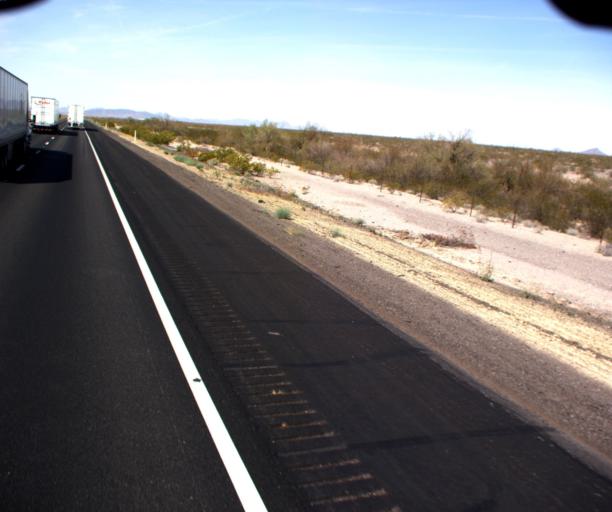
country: US
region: Arizona
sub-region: La Paz County
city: Salome
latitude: 33.6176
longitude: -113.6749
